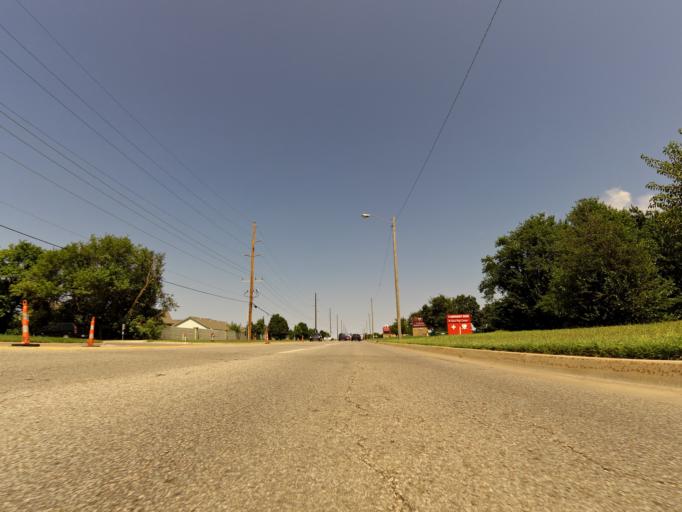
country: US
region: Kansas
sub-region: Sedgwick County
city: Bellaire
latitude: 37.7300
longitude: -97.2623
